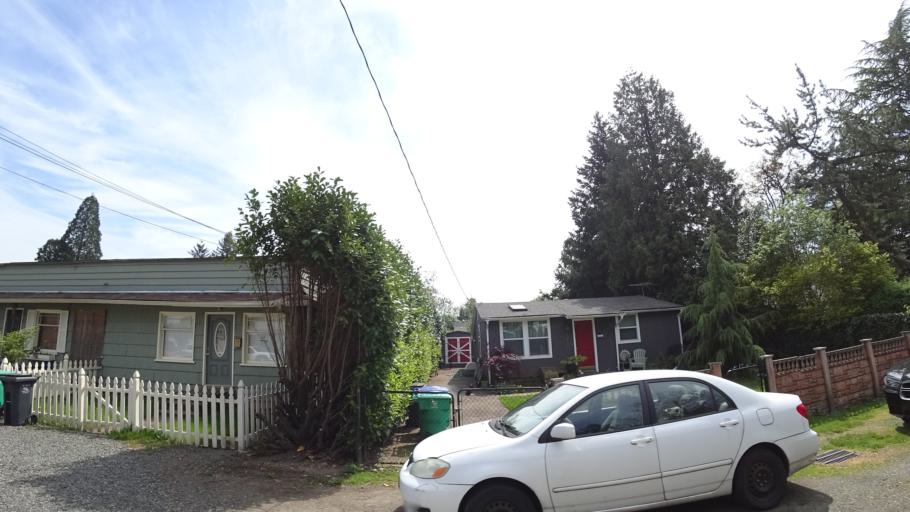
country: US
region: Oregon
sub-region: Multnomah County
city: Lents
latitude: 45.4735
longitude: -122.6066
